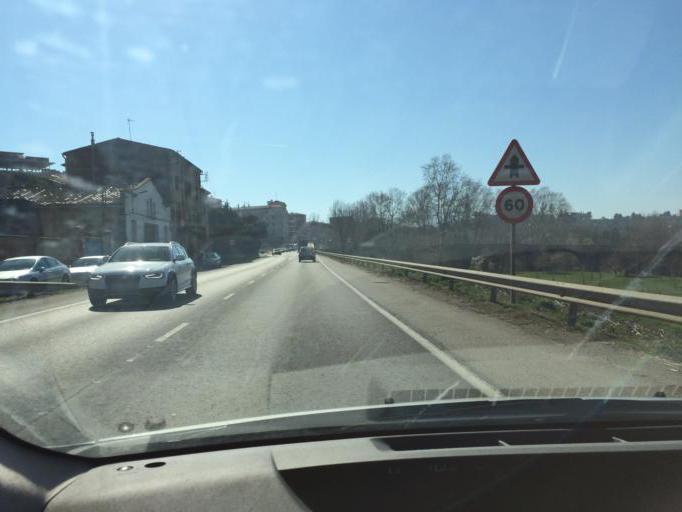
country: ES
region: Catalonia
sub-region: Provincia de Barcelona
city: Manresa
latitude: 41.7298
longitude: 1.8143
